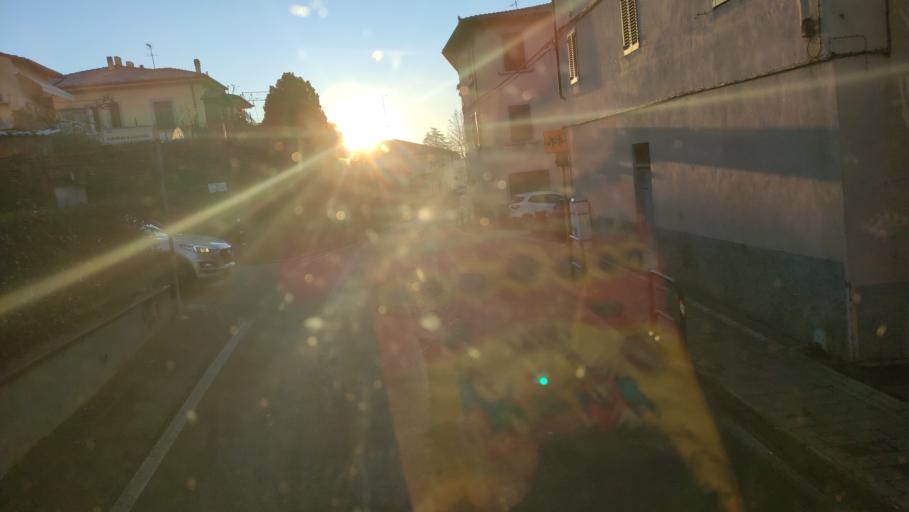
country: IT
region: Tuscany
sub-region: Province of Florence
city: Pozzale-Case Nuove
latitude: 43.6593
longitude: 10.9346
